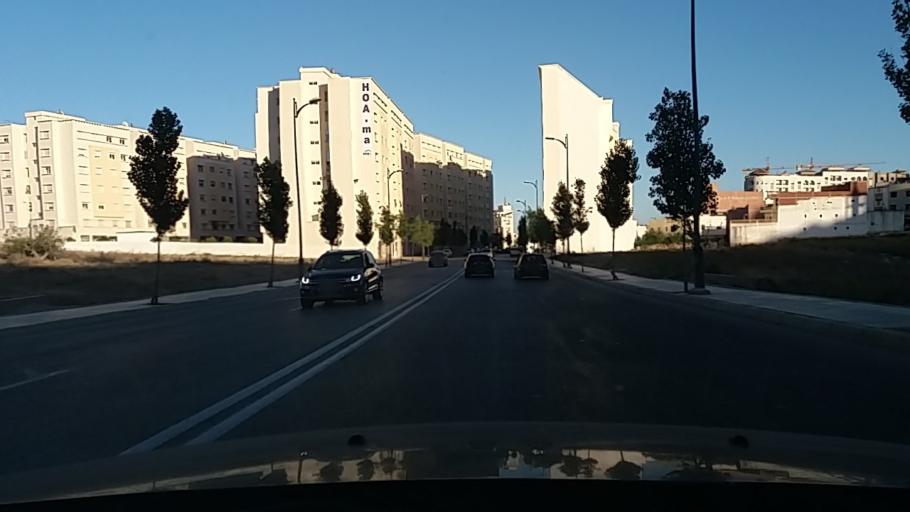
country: MA
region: Tanger-Tetouan
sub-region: Tanger-Assilah
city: Boukhalef
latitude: 35.7675
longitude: -5.8587
